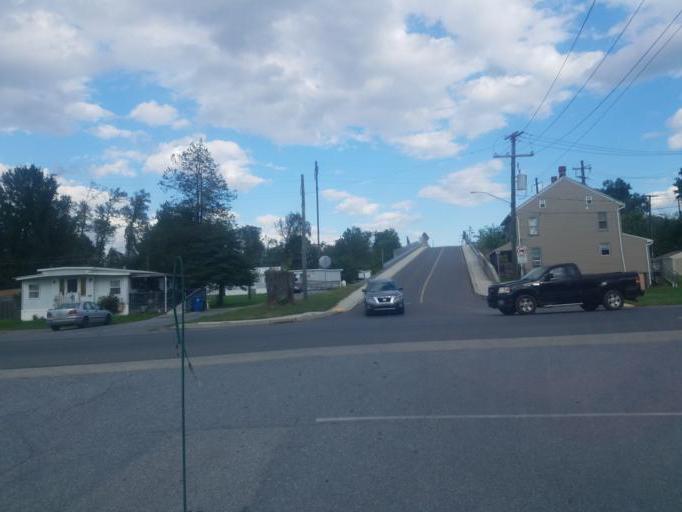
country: US
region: Pennsylvania
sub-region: Dauphin County
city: Middletown
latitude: 40.1884
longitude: -76.7299
